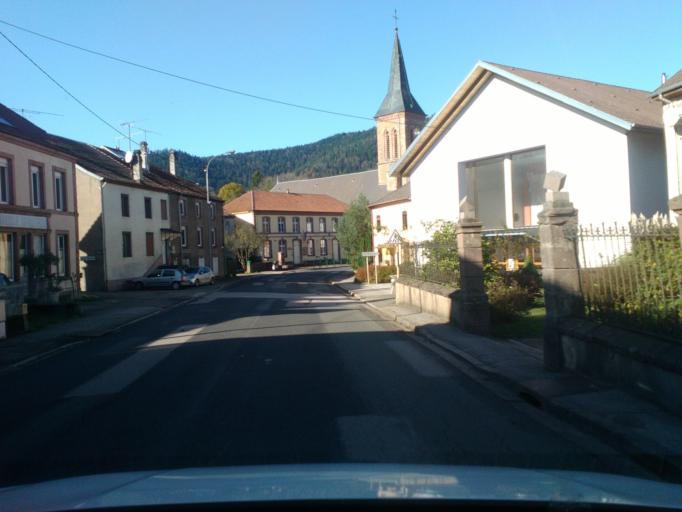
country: FR
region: Lorraine
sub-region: Departement des Vosges
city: Senones
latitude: 48.4053
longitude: 6.9950
